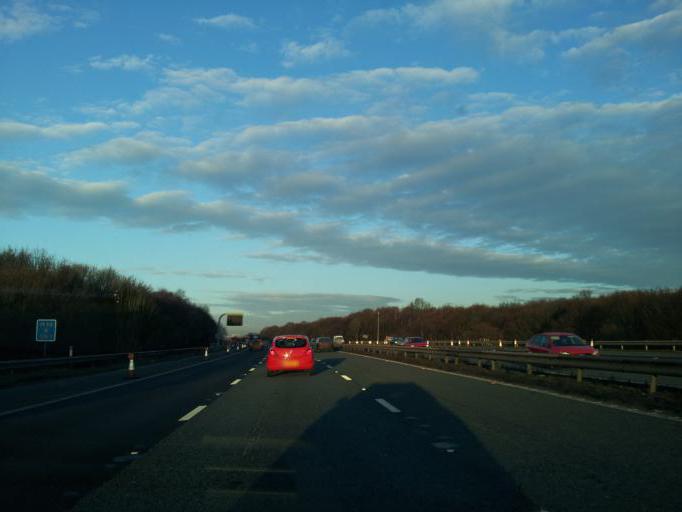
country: GB
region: England
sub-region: City and Borough of Wakefield
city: Castleford
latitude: 53.7075
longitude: -1.3705
